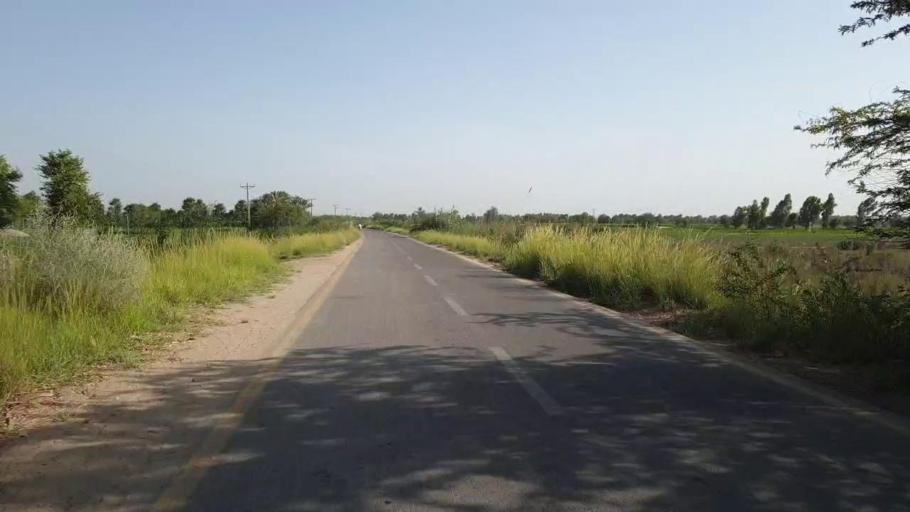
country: PK
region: Sindh
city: Daur
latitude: 26.4611
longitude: 68.4510
